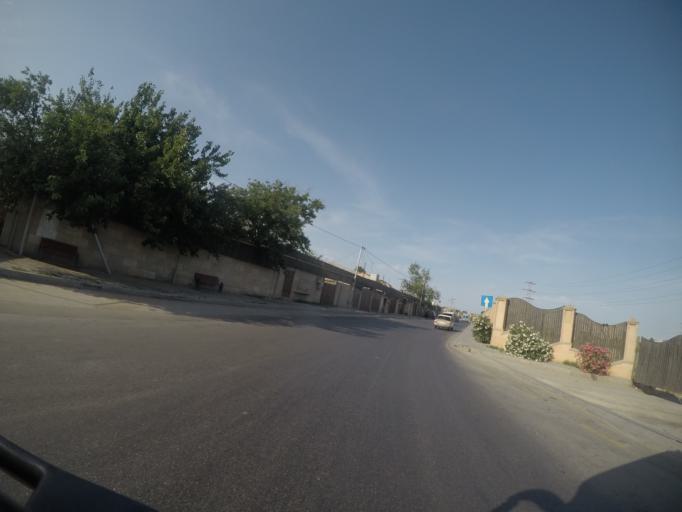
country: AZ
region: Baki
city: Binagadi
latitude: 40.4636
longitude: 49.8413
